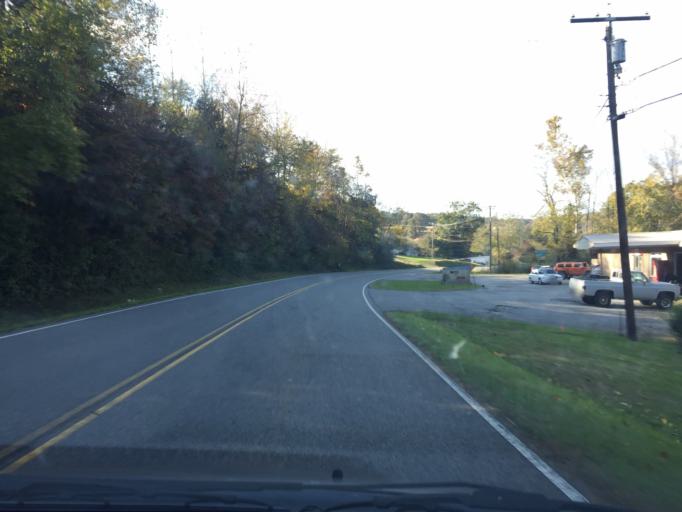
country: US
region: Tennessee
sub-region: Loudon County
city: Loudon
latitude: 35.6995
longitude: -84.3409
